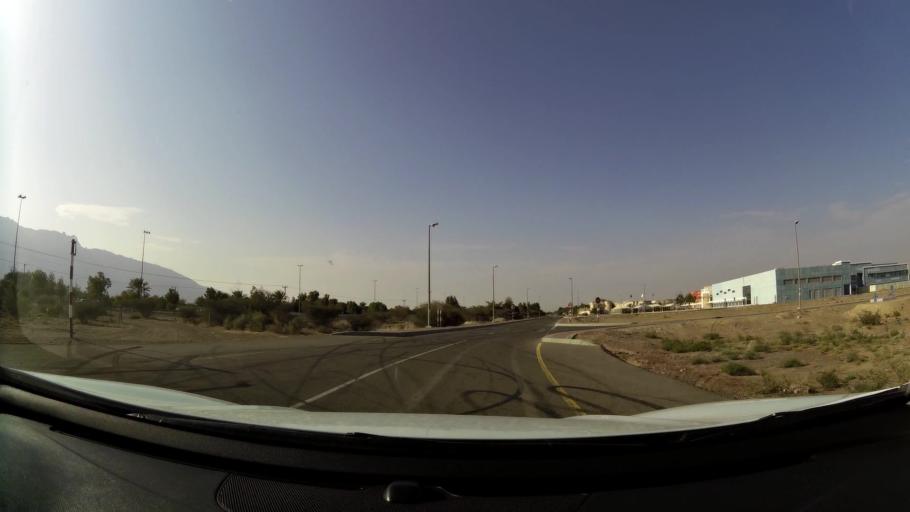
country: AE
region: Abu Dhabi
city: Al Ain
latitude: 24.0469
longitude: 55.8431
